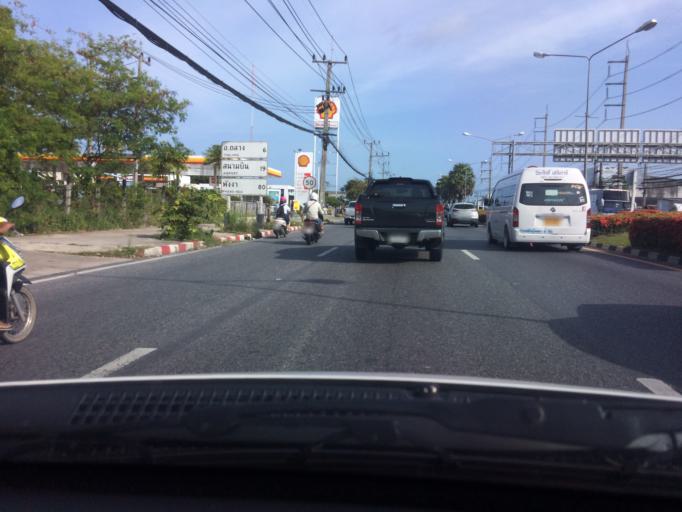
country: TH
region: Phuket
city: Ban Ko Kaeo
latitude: 7.9820
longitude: 98.3628
